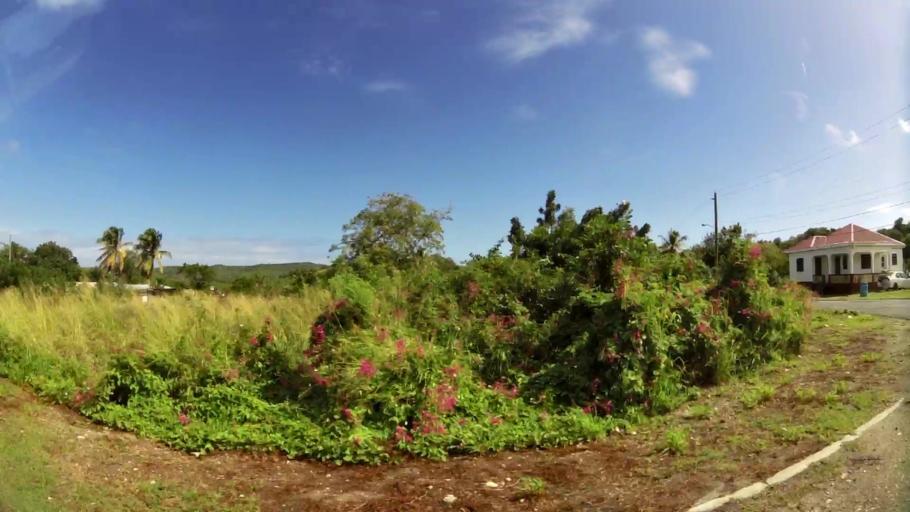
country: AG
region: Saint Paul
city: Falmouth
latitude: 17.0347
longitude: -61.7515
